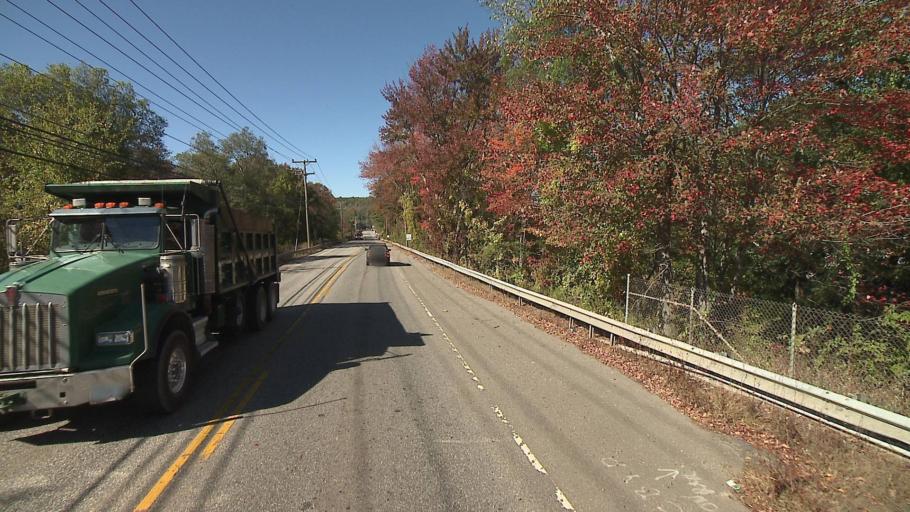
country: US
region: Connecticut
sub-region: Windham County
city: Willimantic
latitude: 41.7168
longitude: -72.2397
